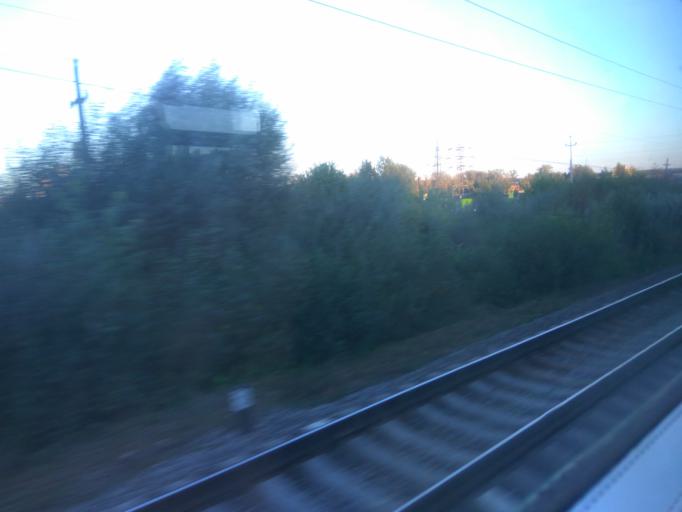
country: RU
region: Moskovskaya
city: Elektrostal'
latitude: 55.7790
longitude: 38.4643
